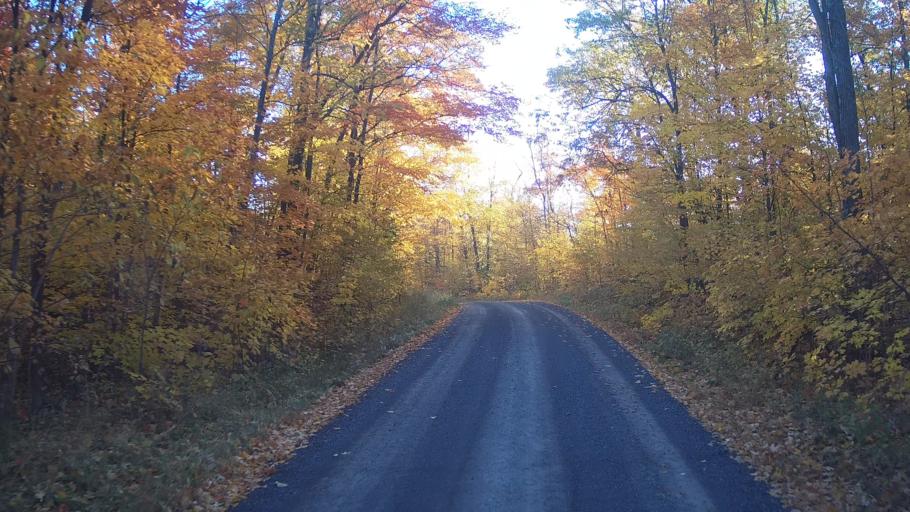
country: CA
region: Ontario
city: Arnprior
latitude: 45.3436
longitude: -76.3436
